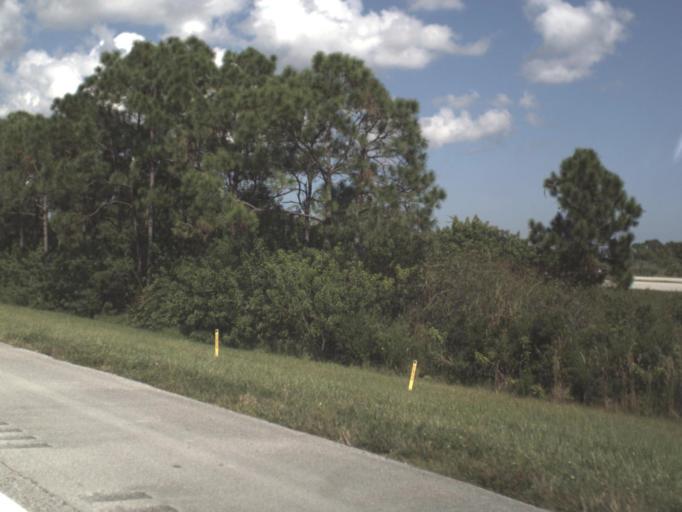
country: US
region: Florida
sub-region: Palm Beach County
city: Tequesta
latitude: 26.9901
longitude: -80.1916
